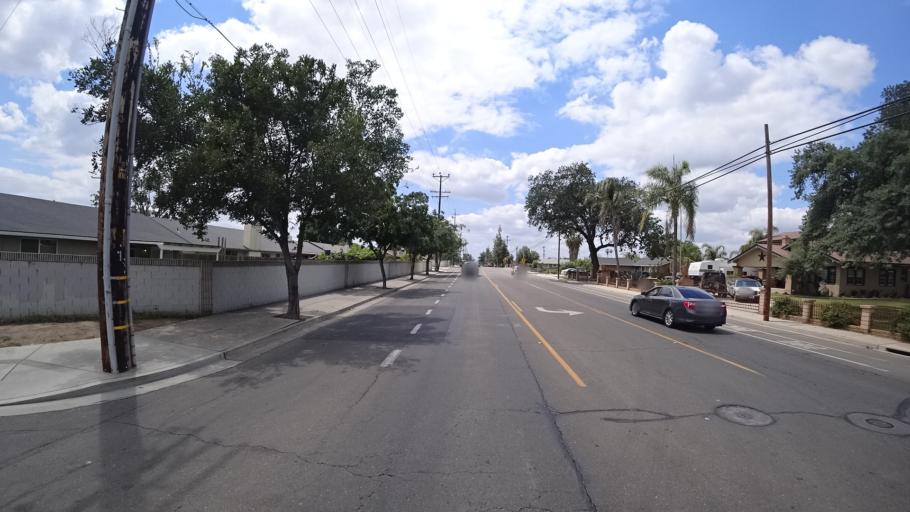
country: US
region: California
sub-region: Kings County
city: Hanford
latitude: 36.3134
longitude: -119.6640
